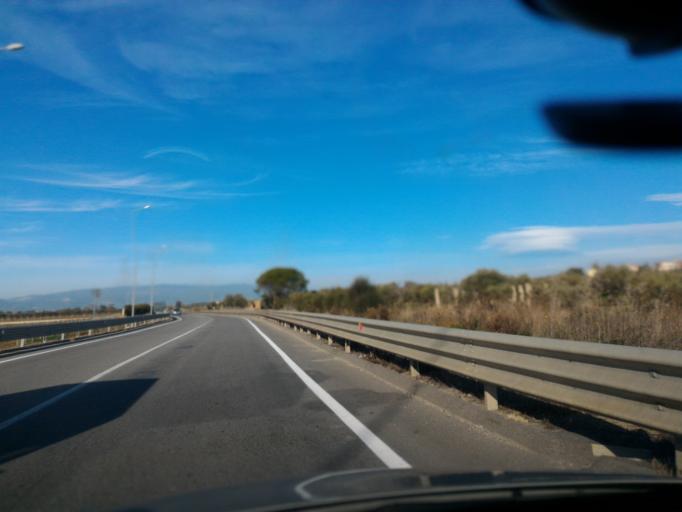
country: IT
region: Calabria
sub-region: Provincia di Crotone
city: Le Castella
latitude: 38.9339
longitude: 17.0095
